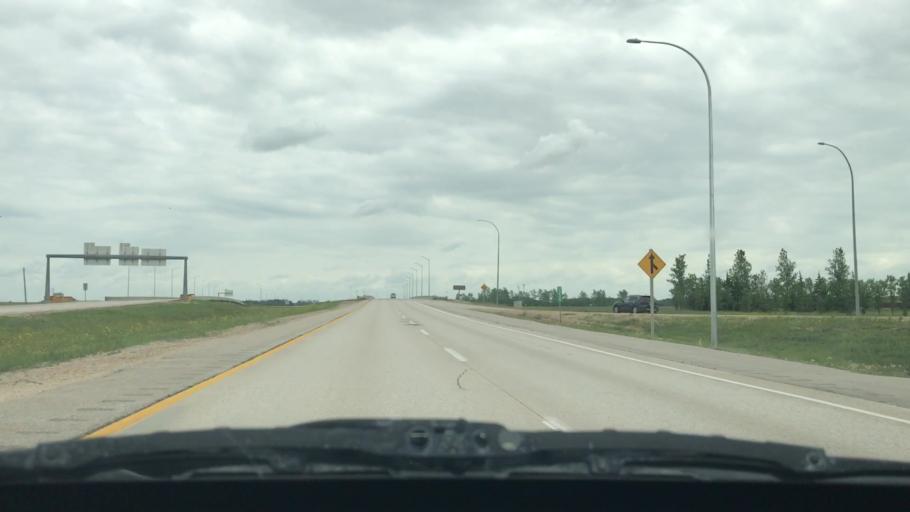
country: CA
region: Manitoba
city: Winnipeg
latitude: 49.8331
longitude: -96.9602
